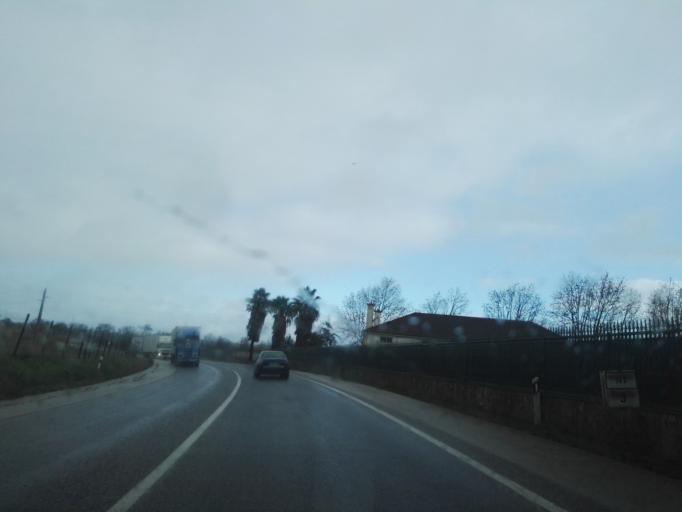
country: PT
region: Lisbon
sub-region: Alenquer
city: Carregado
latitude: 39.0321
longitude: -8.9471
